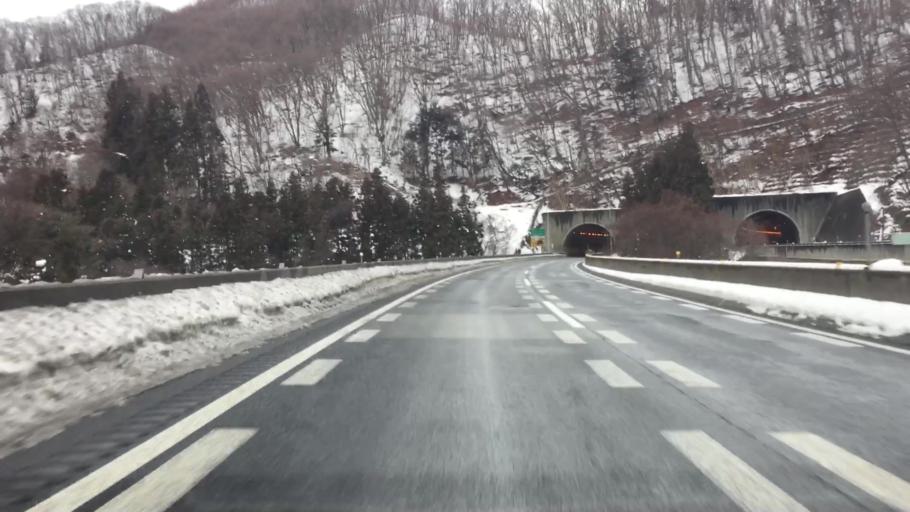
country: JP
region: Gunma
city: Numata
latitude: 36.7530
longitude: 138.9684
